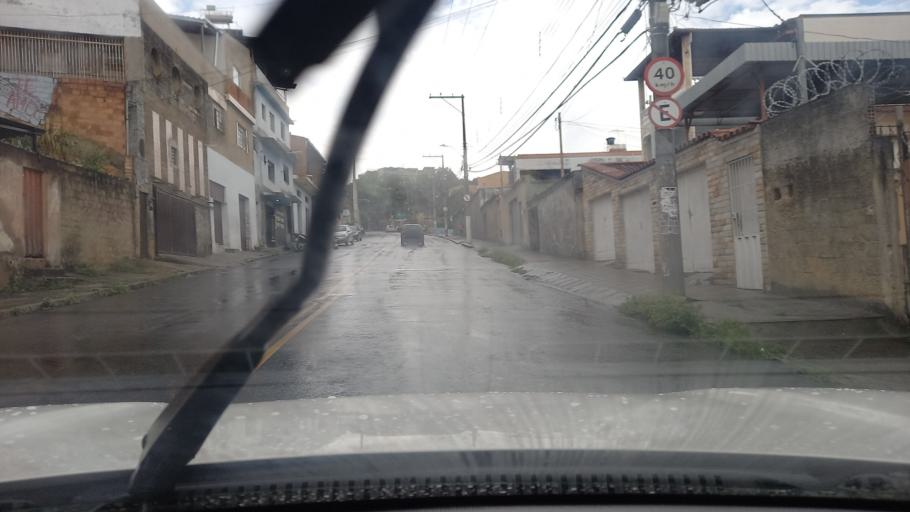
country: BR
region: Minas Gerais
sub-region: Belo Horizonte
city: Belo Horizonte
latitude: -19.9049
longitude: -43.9490
